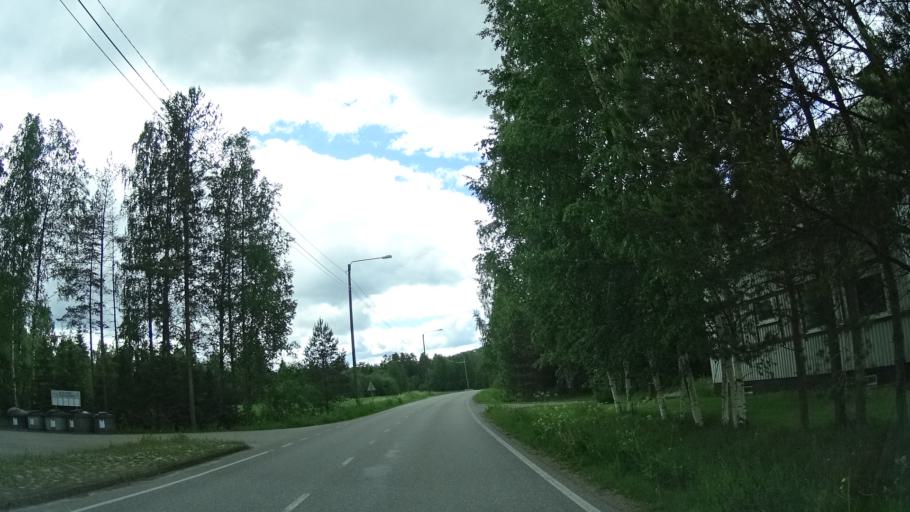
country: FI
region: Central Finland
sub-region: Jyvaeskylae
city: Toivakka
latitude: 61.9927
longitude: 25.9722
